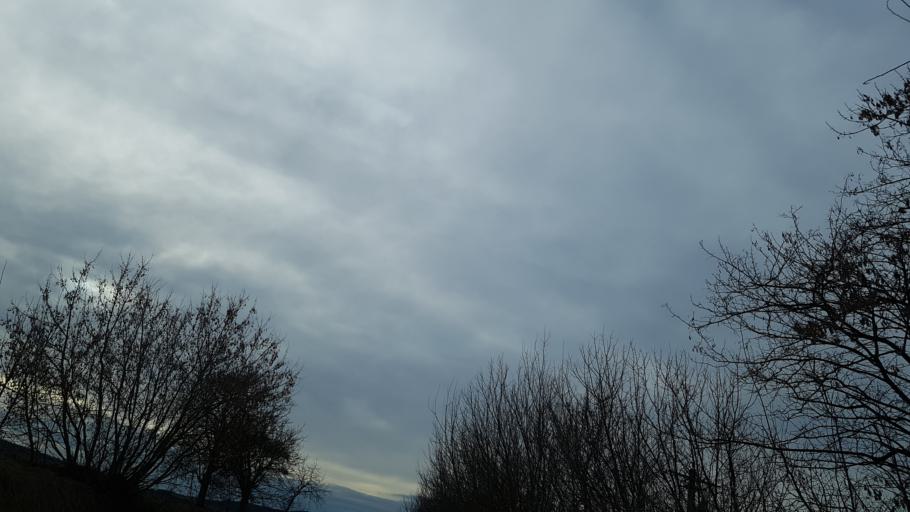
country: RO
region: Sibiu
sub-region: Comuna Micasasa
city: Micasasa
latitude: 46.0783
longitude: 24.1217
